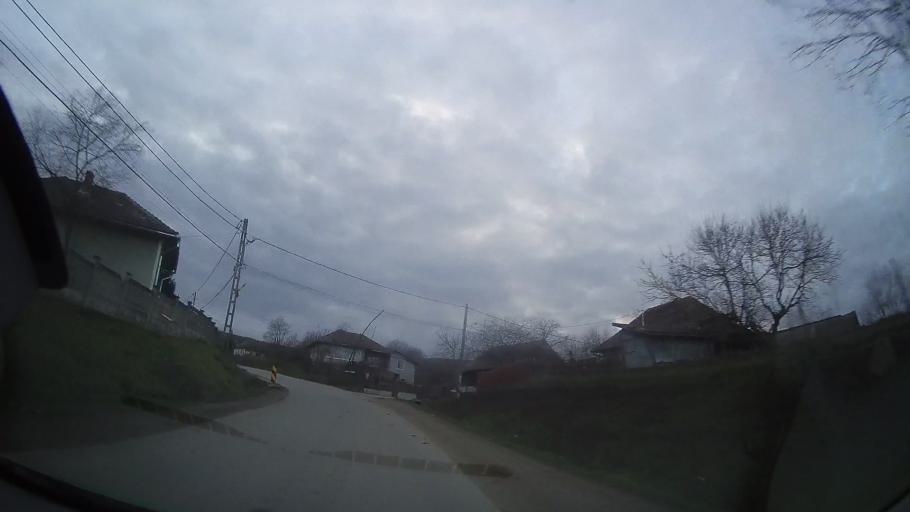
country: RO
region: Cluj
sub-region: Comuna Palatca
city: Palatca
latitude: 46.8391
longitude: 23.9843
